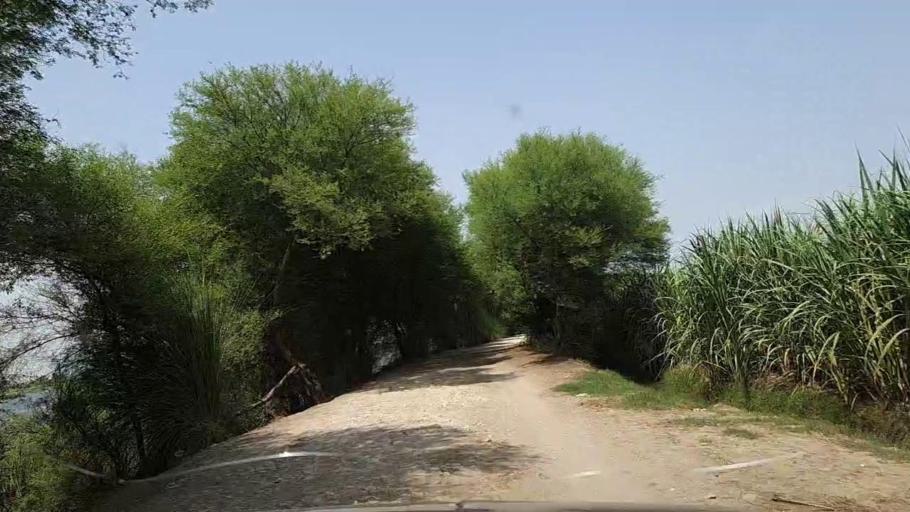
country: PK
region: Sindh
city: Ghotki
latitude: 28.0892
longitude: 69.3109
